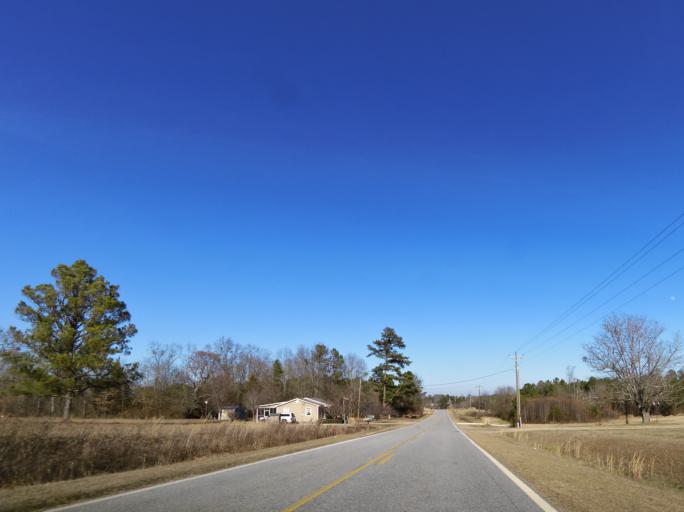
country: US
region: Georgia
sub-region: Bibb County
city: West Point
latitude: 32.7575
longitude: -83.8830
